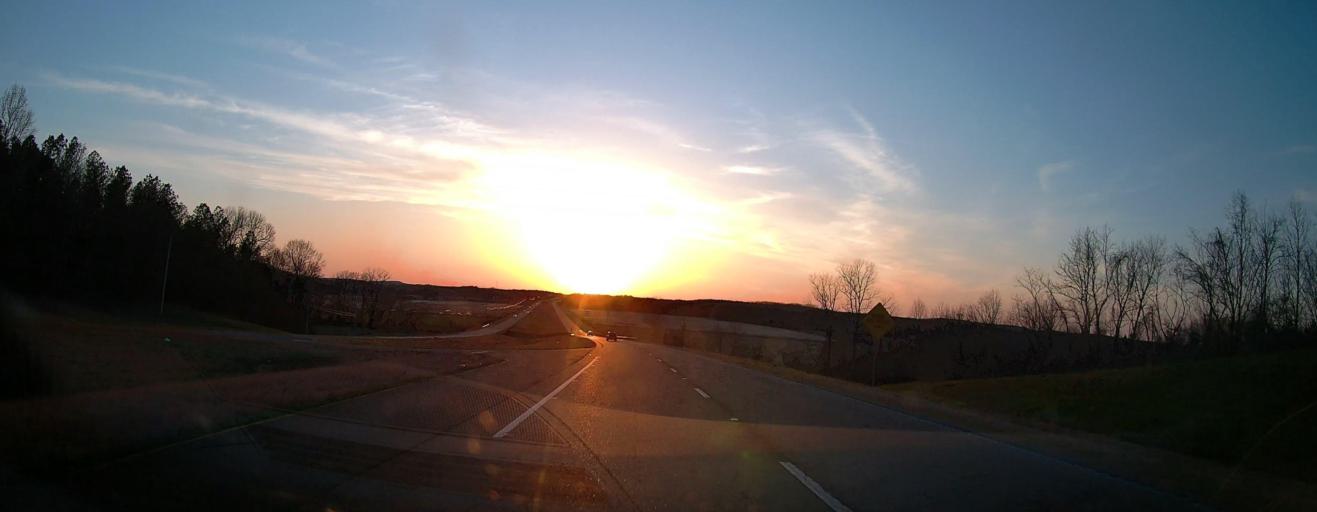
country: US
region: Mississippi
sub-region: Alcorn County
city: Corinth
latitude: 34.9327
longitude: -88.6490
